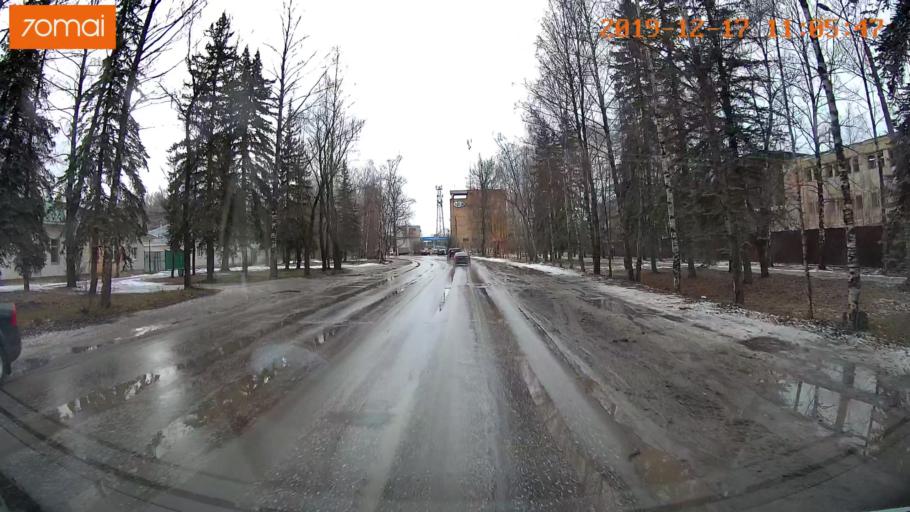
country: RU
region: Vladimir
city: Gus'-Khrustal'nyy
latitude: 55.6190
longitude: 40.6429
